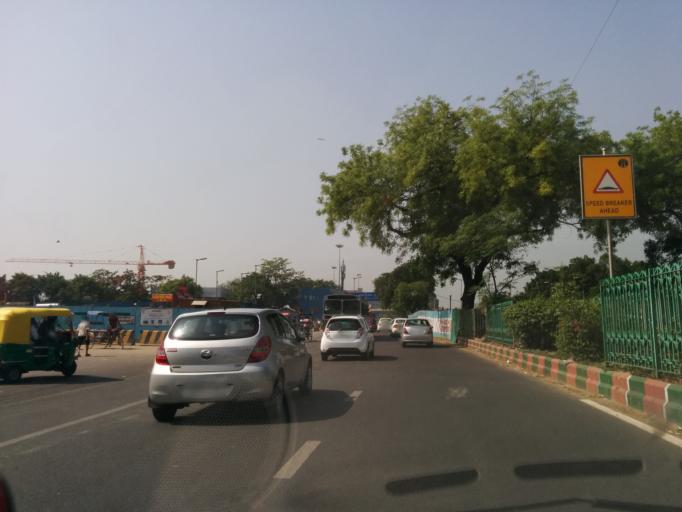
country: IN
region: NCT
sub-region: New Delhi
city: New Delhi
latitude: 28.5740
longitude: 77.2095
